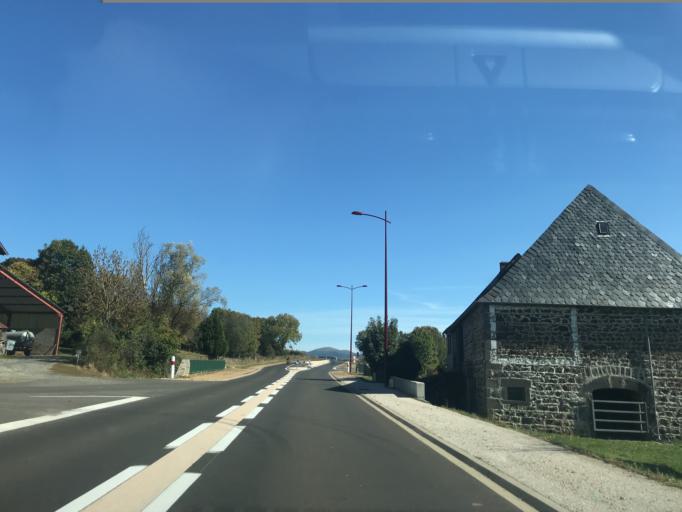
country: FR
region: Auvergne
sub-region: Departement du Puy-de-Dome
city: Gelles
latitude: 45.7336
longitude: 2.8367
